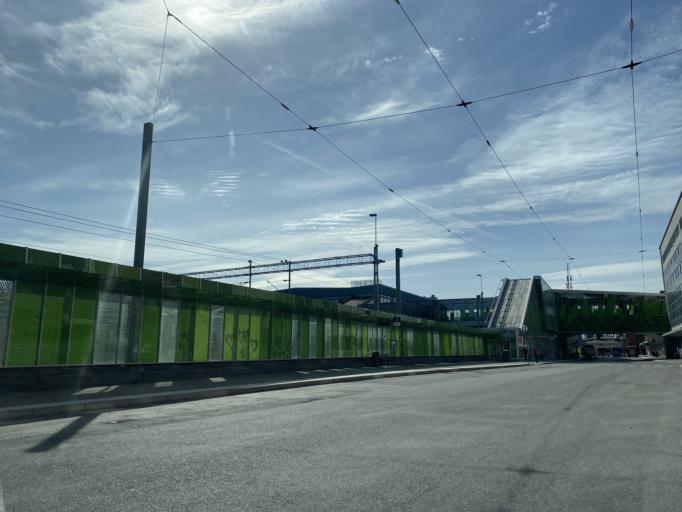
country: SE
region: Stockholm
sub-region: Stockholms Kommun
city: Arsta
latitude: 59.2795
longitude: 18.0120
